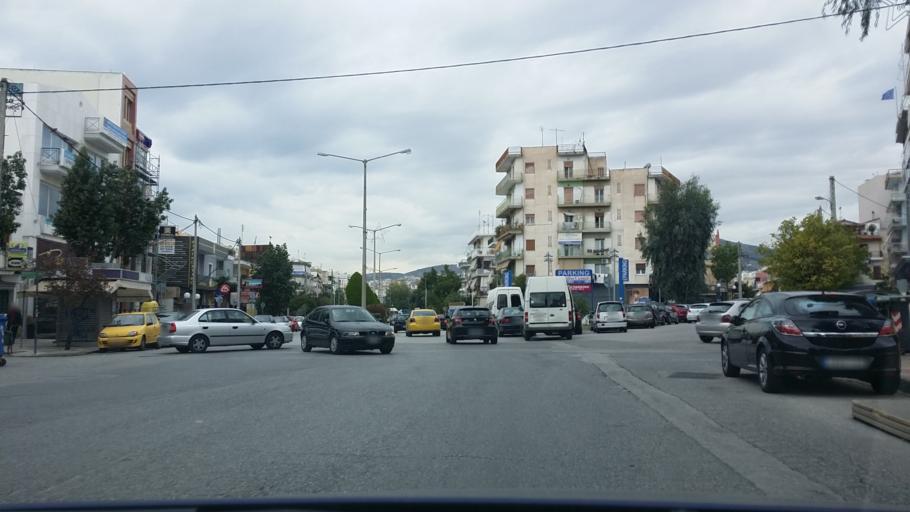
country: GR
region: Attica
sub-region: Nomarchia Athinas
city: Peristeri
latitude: 38.0115
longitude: 23.6903
